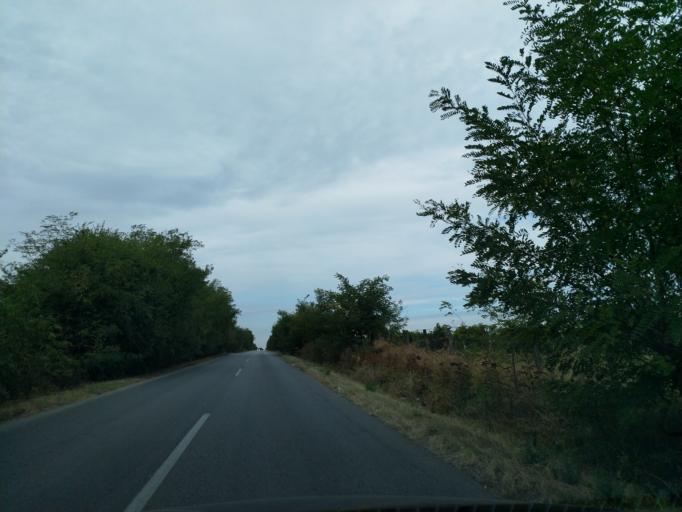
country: RS
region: Central Serbia
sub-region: Pomoravski Okrug
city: Jagodina
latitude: 43.9960
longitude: 21.2211
